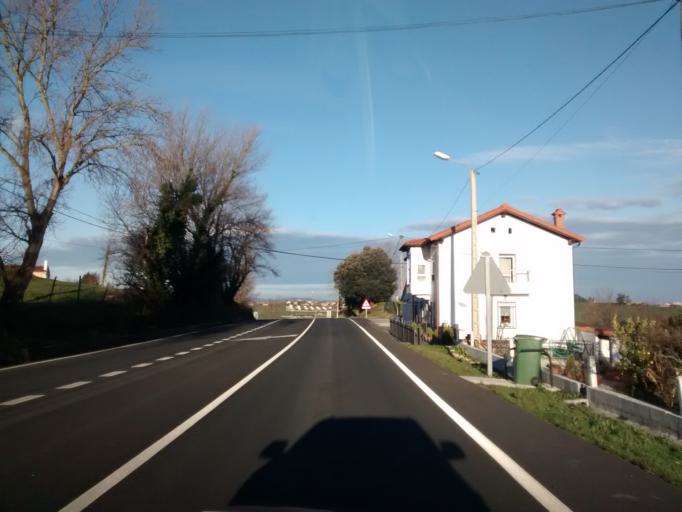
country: ES
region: Cantabria
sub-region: Provincia de Cantabria
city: El Astillero
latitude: 43.3979
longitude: -3.7731
